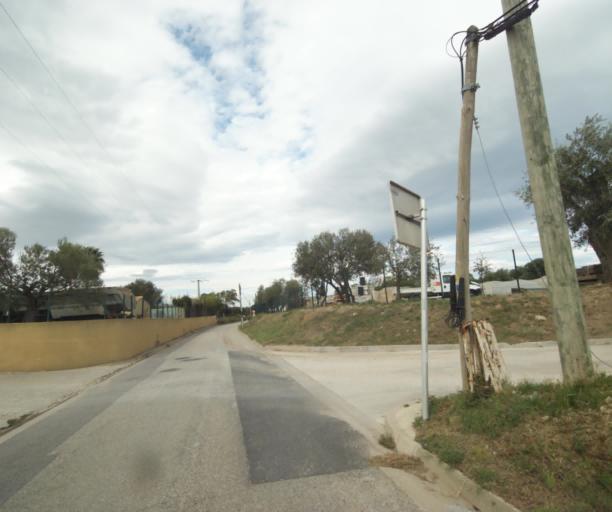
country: FR
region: Languedoc-Roussillon
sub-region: Departement des Pyrenees-Orientales
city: Sant Andreu de Sureda
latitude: 42.5492
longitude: 2.9910
